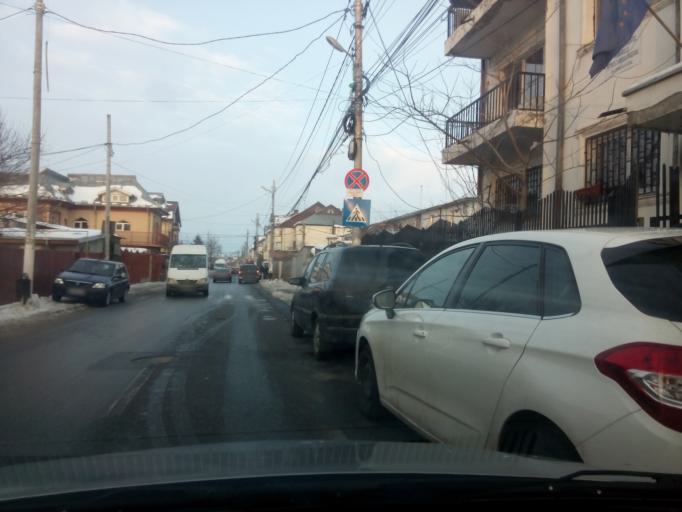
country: RO
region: Ilfov
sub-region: Comuna Pantelimon
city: Pantelimon
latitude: 44.4541
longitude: 26.2066
